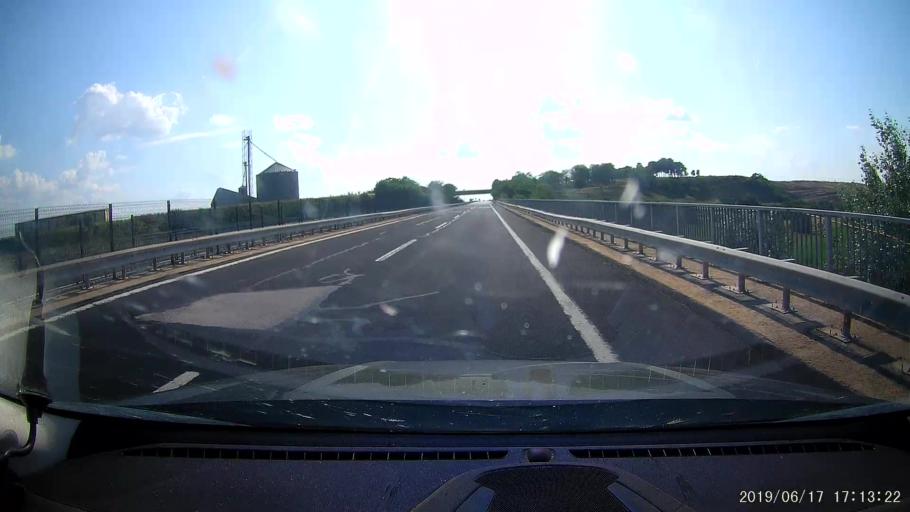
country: TR
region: Edirne
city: Edirne
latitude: 41.7009
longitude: 26.5415
